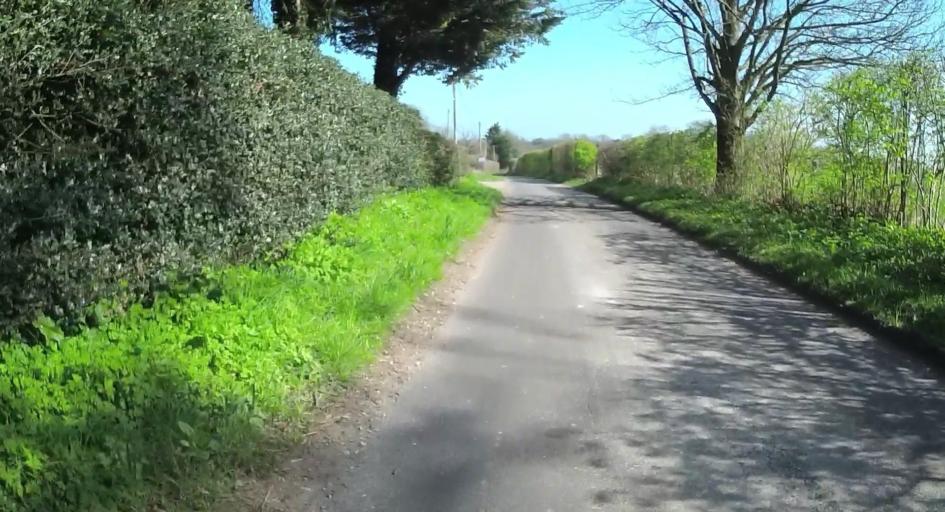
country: GB
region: England
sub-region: Hampshire
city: Highclere
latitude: 51.2803
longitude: -1.4058
